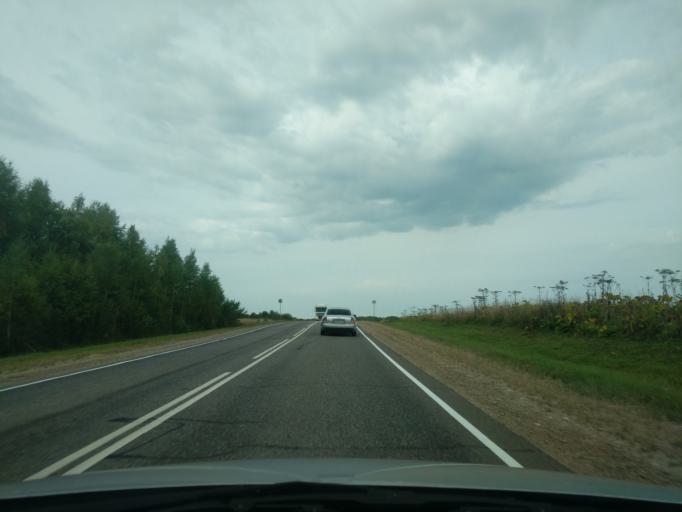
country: RU
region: Kirov
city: Mirnyy
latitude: 58.2733
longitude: 47.7730
